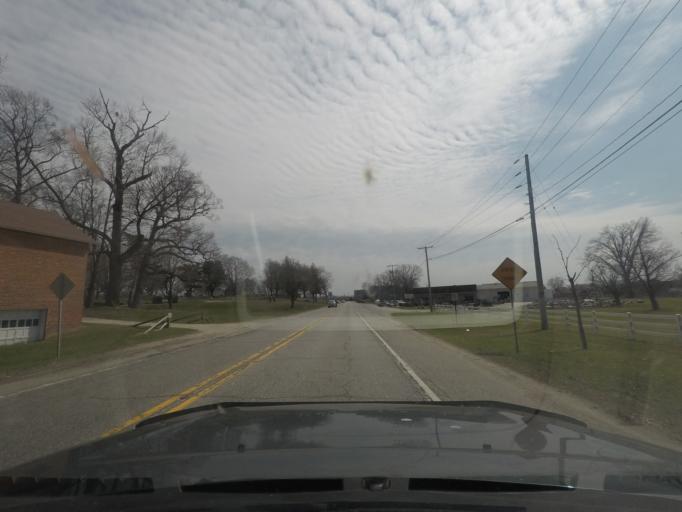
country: US
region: Indiana
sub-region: LaPorte County
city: LaPorte
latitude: 41.6374
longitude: -86.7457
